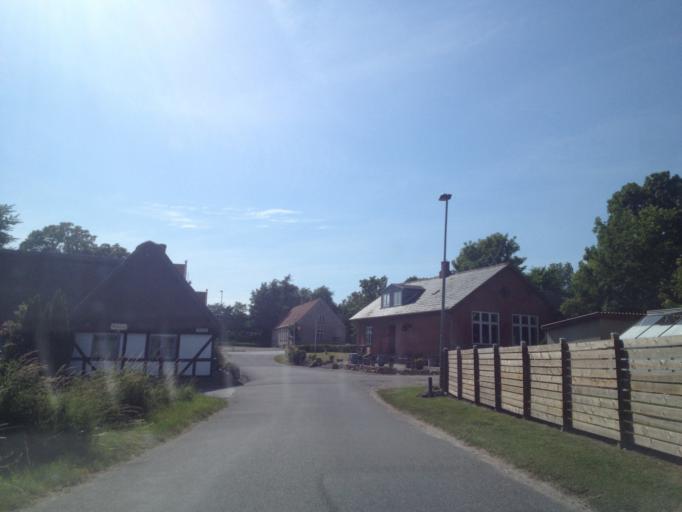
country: DK
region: Central Jutland
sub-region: Samso Kommune
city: Tranebjerg
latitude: 55.8006
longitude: 10.5596
